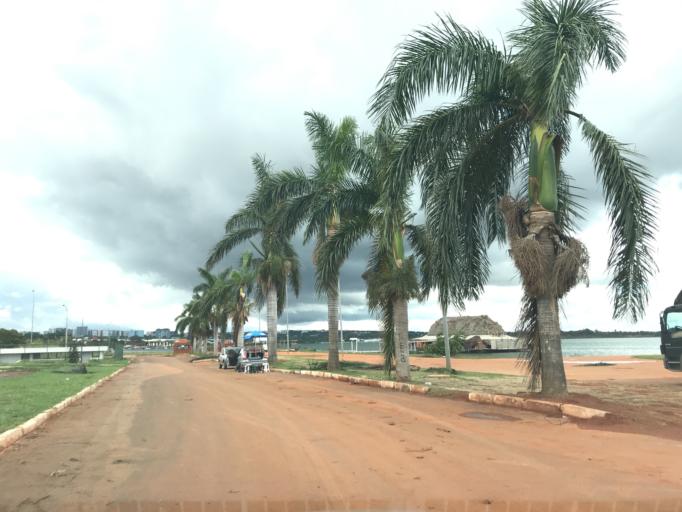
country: BR
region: Federal District
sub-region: Brasilia
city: Brasilia
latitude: -15.7861
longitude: -47.8365
